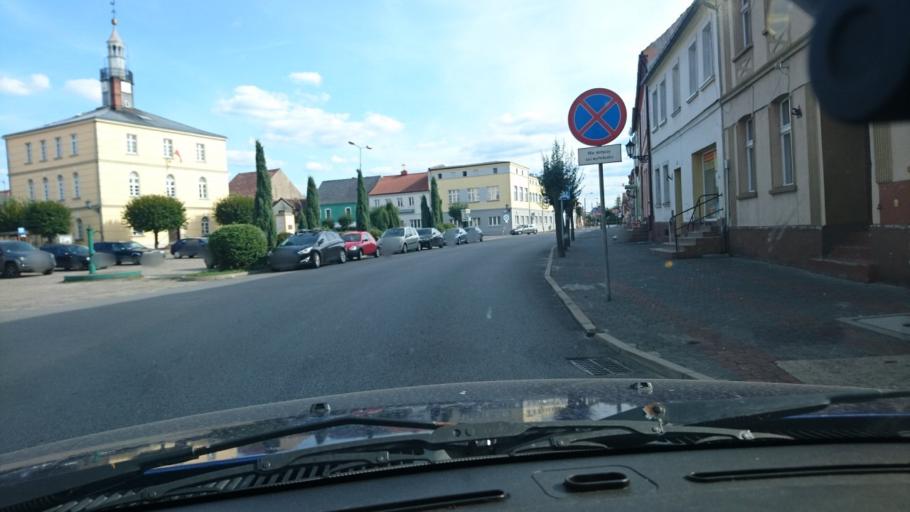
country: PL
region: Greater Poland Voivodeship
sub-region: Powiat rawicki
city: Jutrosin
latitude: 51.6541
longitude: 17.1685
